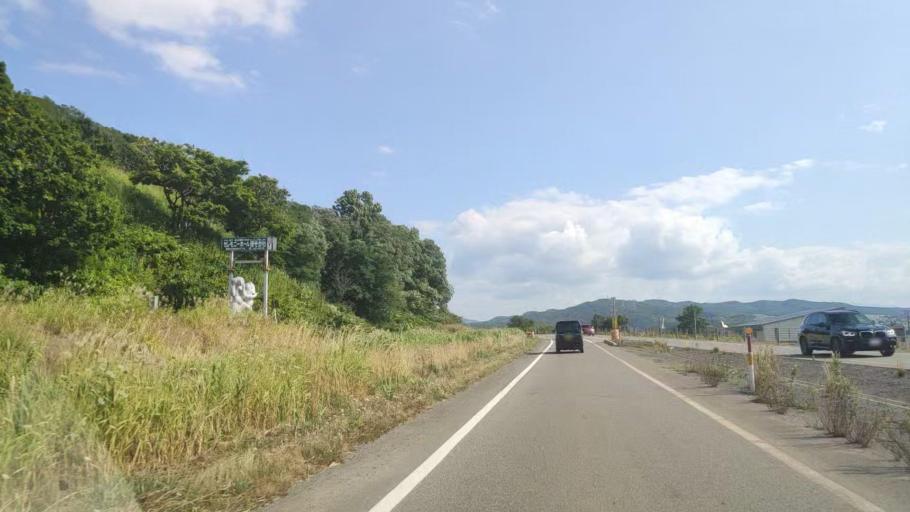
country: JP
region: Hokkaido
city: Rumoi
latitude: 43.9523
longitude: 141.6454
